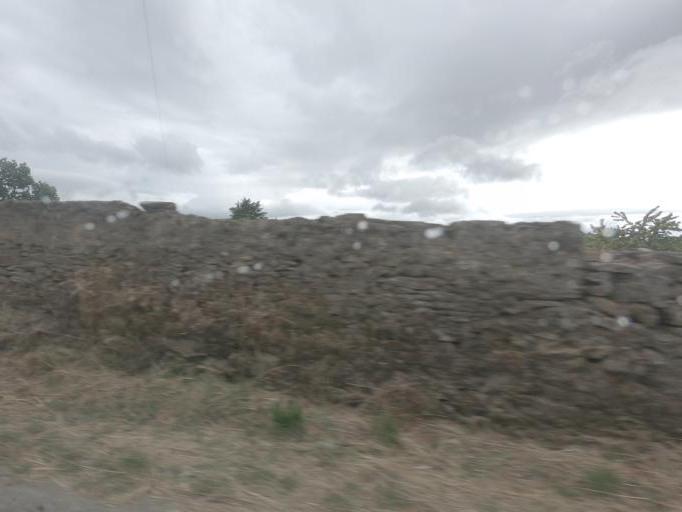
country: PT
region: Vila Real
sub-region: Sabrosa
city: Sabrosa
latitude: 41.2534
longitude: -7.5012
